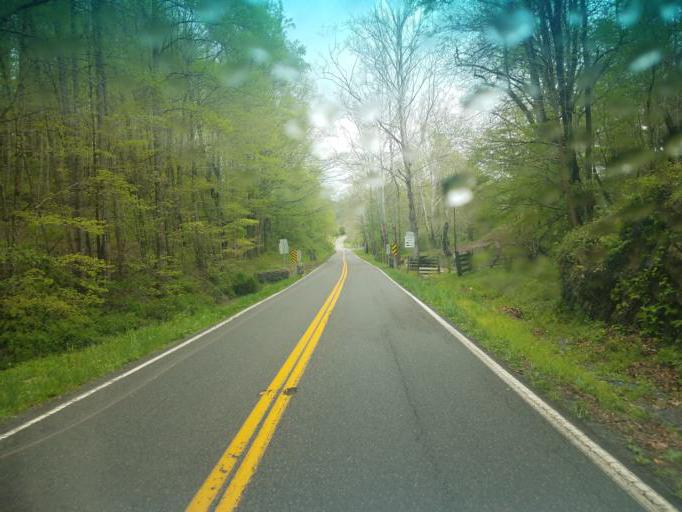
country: US
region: Virginia
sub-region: Smyth County
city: Marion
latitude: 36.9452
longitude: -81.5311
